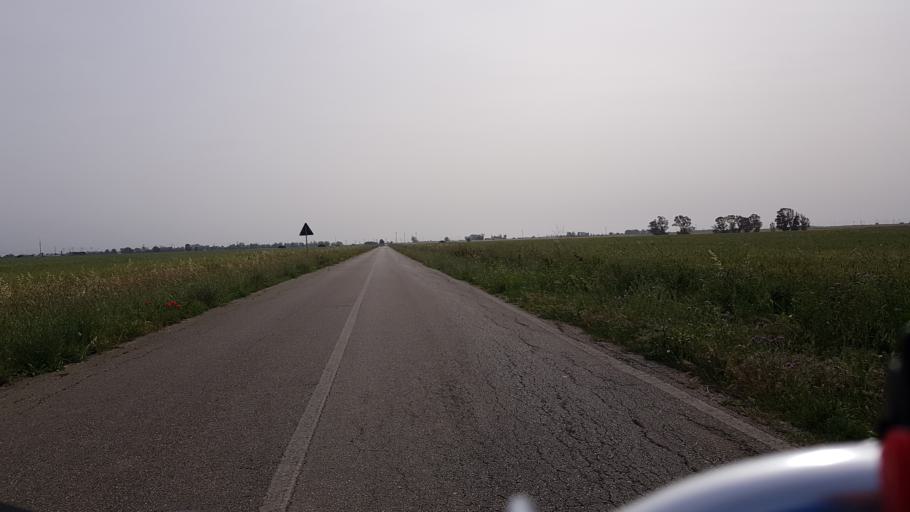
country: IT
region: Apulia
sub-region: Provincia di Brindisi
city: La Rosa
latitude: 40.5808
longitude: 18.0304
